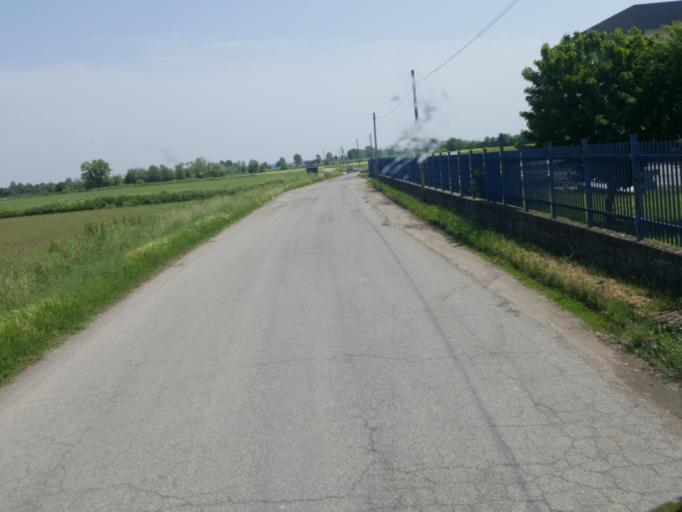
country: IT
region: Lombardy
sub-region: Provincia di Lodi
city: Boffalora d'Adda
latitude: 45.3589
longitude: 9.5038
